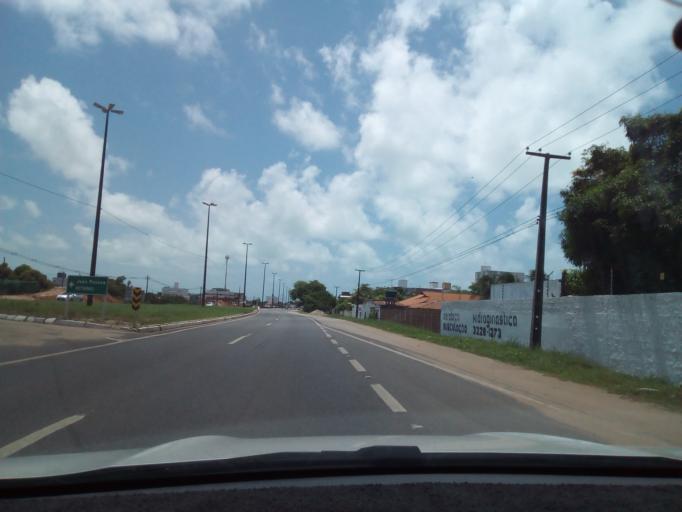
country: BR
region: Paraiba
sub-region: Cabedelo
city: Cabedelo
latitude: -7.0118
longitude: -34.8319
